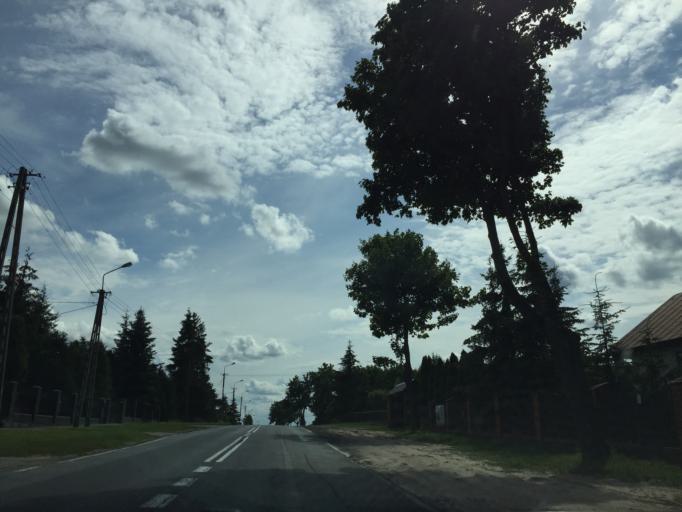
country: PL
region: Masovian Voivodeship
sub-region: Powiat losicki
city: Losice
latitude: 52.2148
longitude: 22.7305
